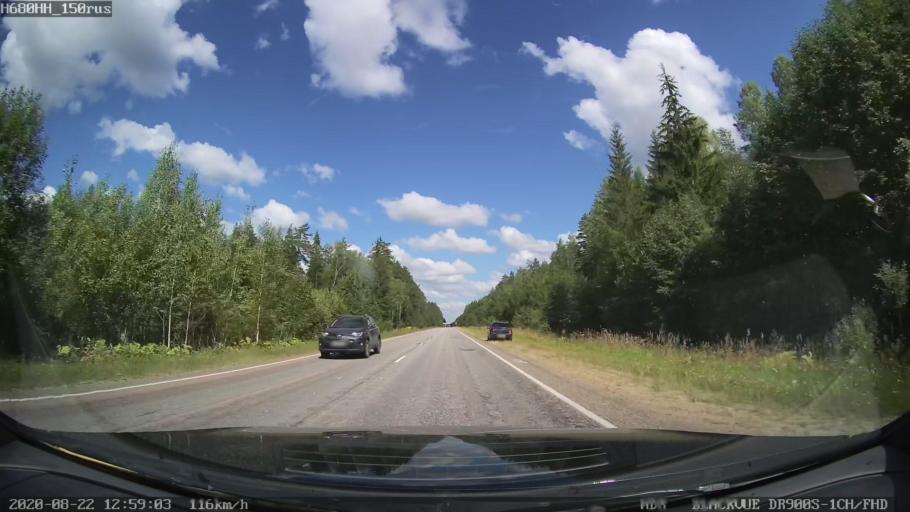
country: RU
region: Tverskaya
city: Bezhetsk
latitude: 57.5998
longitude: 36.3543
